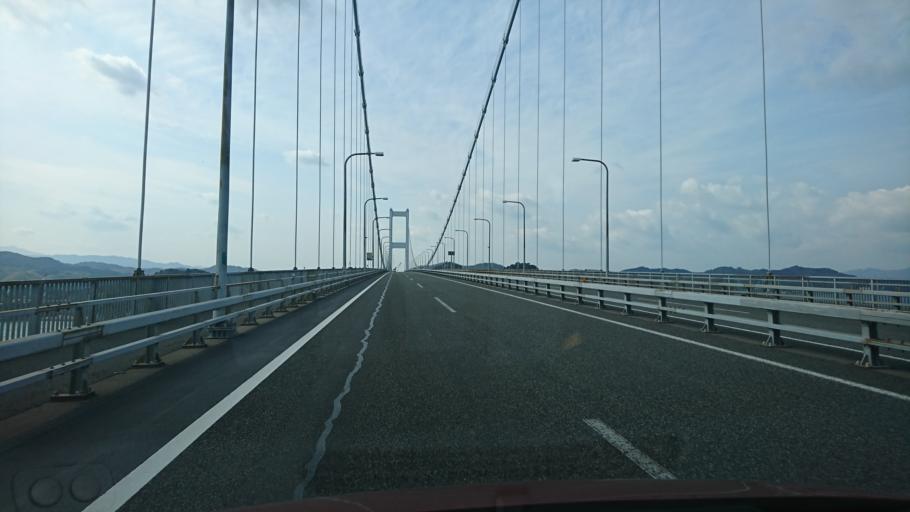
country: JP
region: Hiroshima
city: Takehara
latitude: 34.1168
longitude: 132.9887
